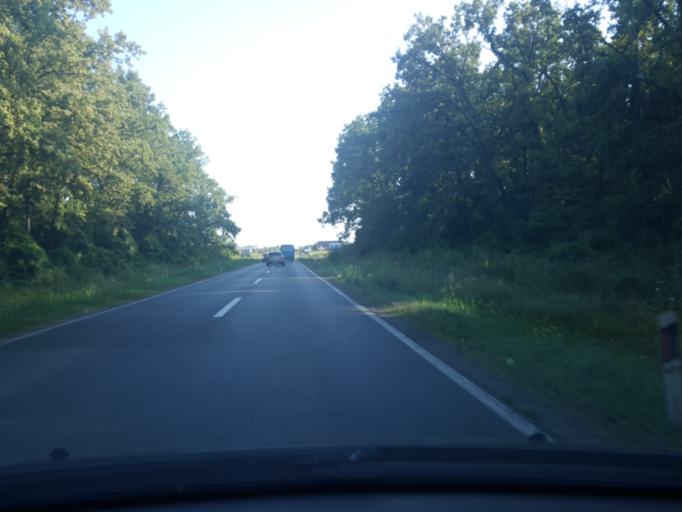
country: RS
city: Hrtkovci
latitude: 44.8950
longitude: 19.7641
